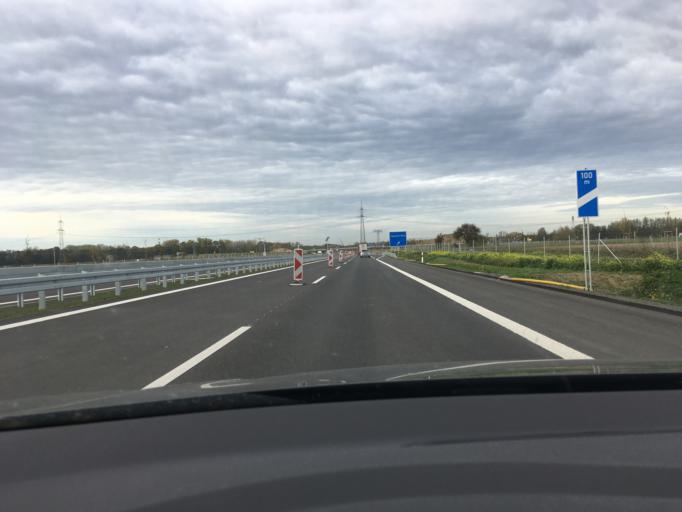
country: DE
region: Saxony
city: Espenhain
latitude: 51.1909
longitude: 12.4483
